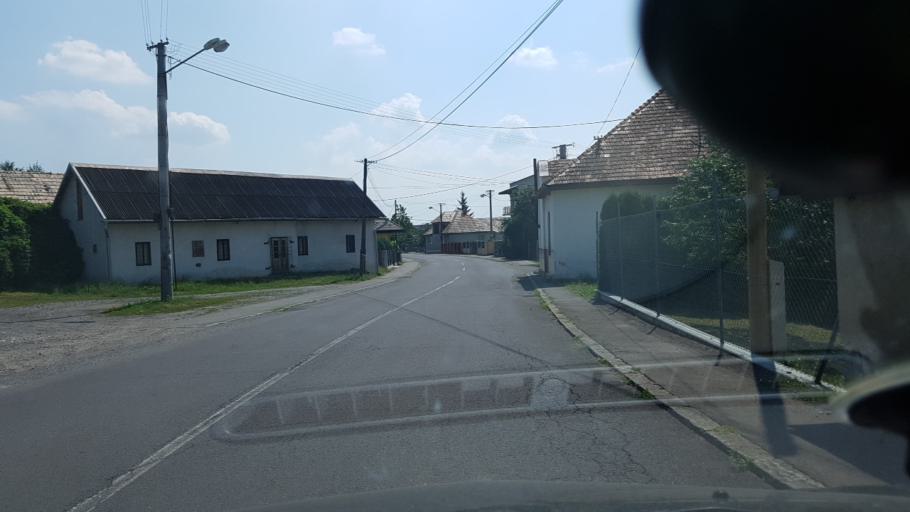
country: SK
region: Banskobystricky
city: Velky Krtis
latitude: 48.2814
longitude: 19.4233
